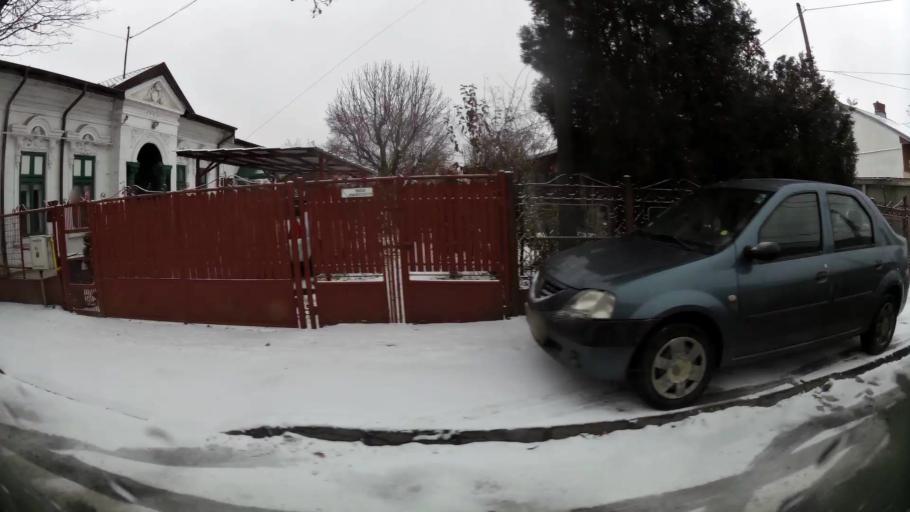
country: RO
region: Prahova
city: Ploiesti
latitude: 44.9343
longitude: 26.0073
